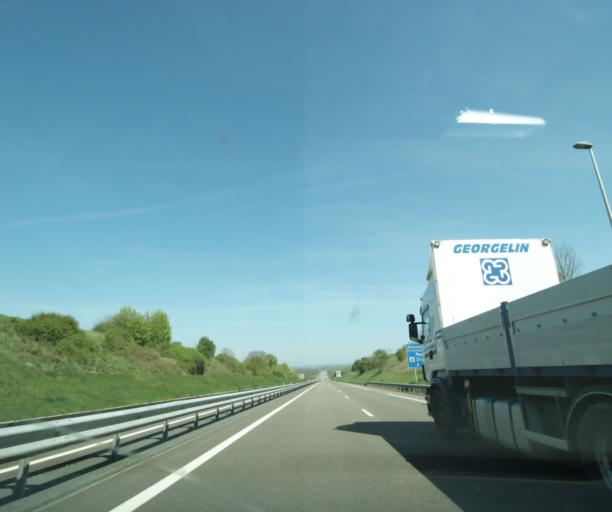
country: FR
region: Bourgogne
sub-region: Departement de la Nievre
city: Challuy
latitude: 46.9437
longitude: 3.1623
